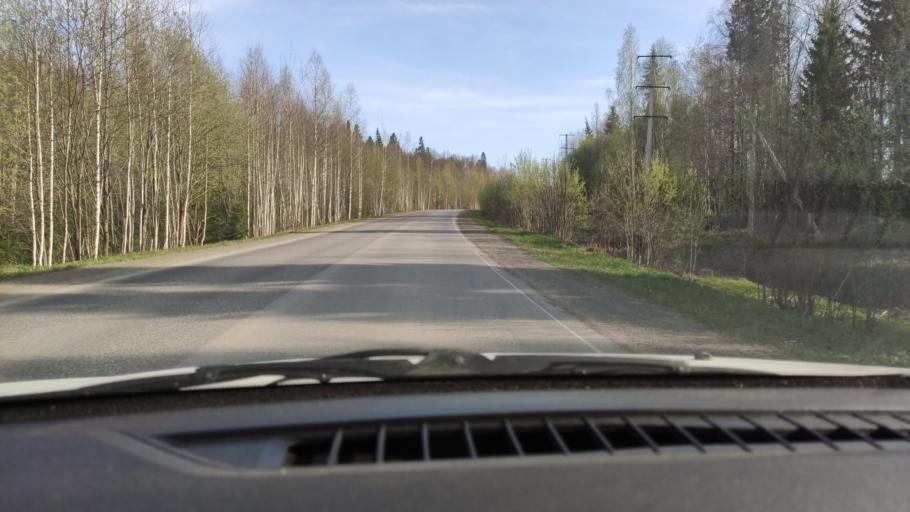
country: RU
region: Perm
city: Novyye Lyady
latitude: 57.9534
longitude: 56.5683
